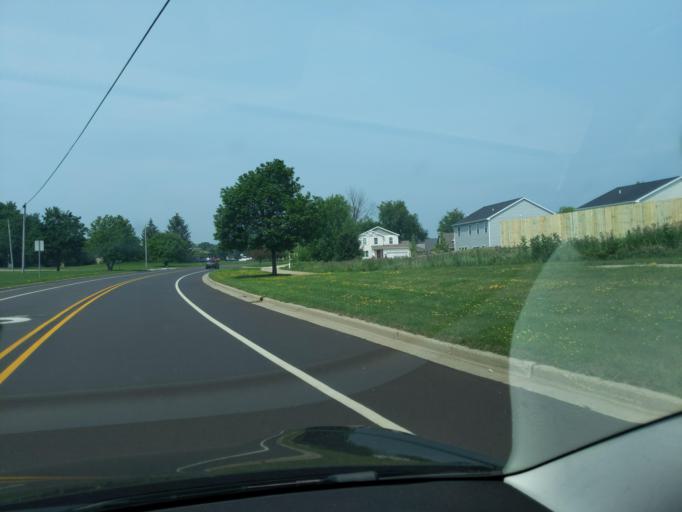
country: US
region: Michigan
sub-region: Clinton County
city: DeWitt
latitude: 42.8331
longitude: -84.5724
